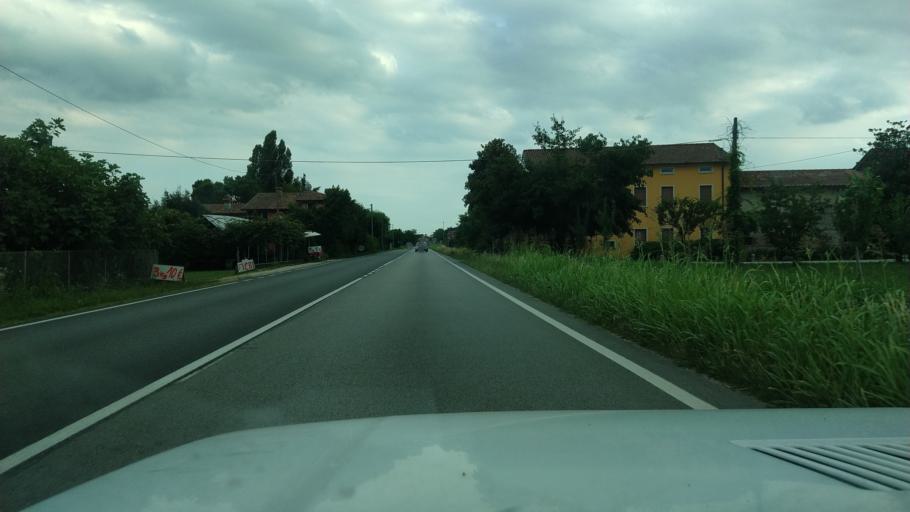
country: IT
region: Veneto
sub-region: Provincia di Vicenza
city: Schiavon
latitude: 45.7133
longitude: 11.6496
